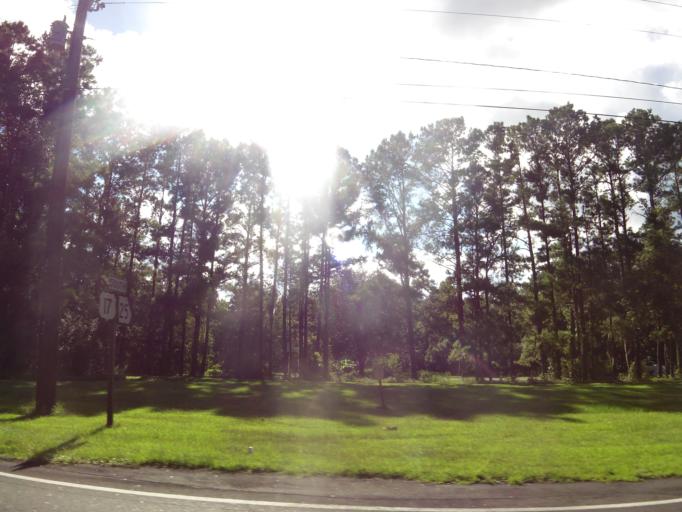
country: US
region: Georgia
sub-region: Camden County
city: Woodbine
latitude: 31.0305
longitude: -81.7306
